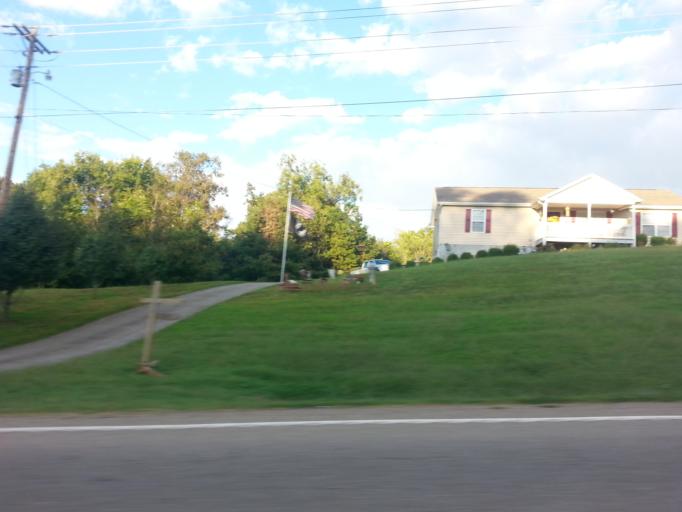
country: US
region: Tennessee
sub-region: Jefferson County
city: Jefferson City
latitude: 36.1441
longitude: -83.5259
